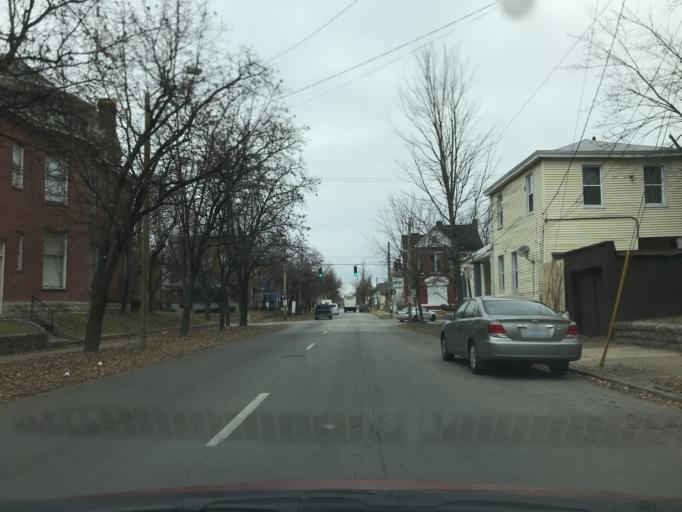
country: US
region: Kentucky
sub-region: Jefferson County
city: Louisville
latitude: 38.2516
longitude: -85.7861
